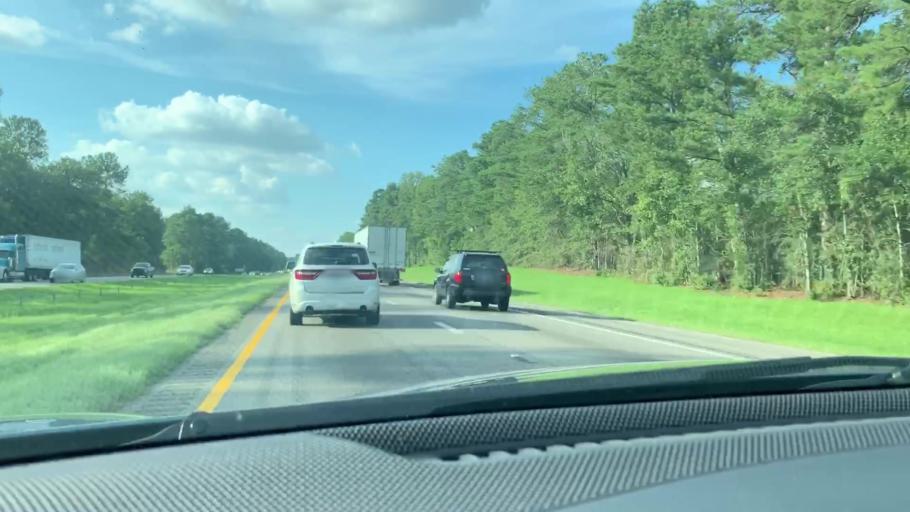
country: US
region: South Carolina
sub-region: Orangeburg County
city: Brookdale
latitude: 33.5441
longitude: -80.8117
